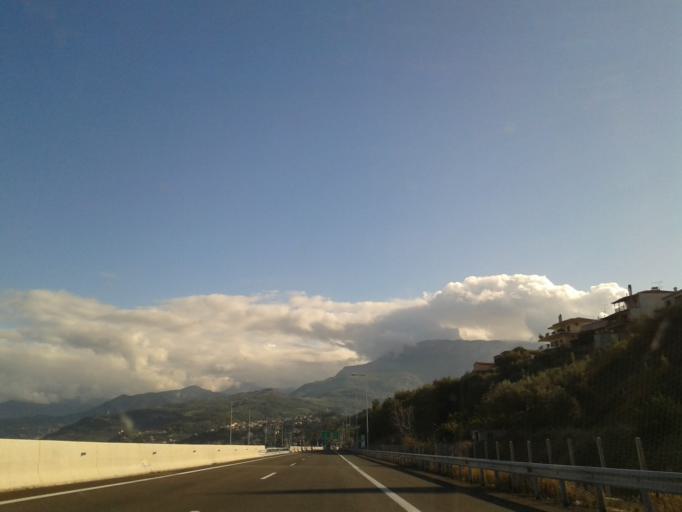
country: GR
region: West Greece
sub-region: Nomos Achaias
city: Siliveniotika
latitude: 38.1620
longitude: 22.3365
